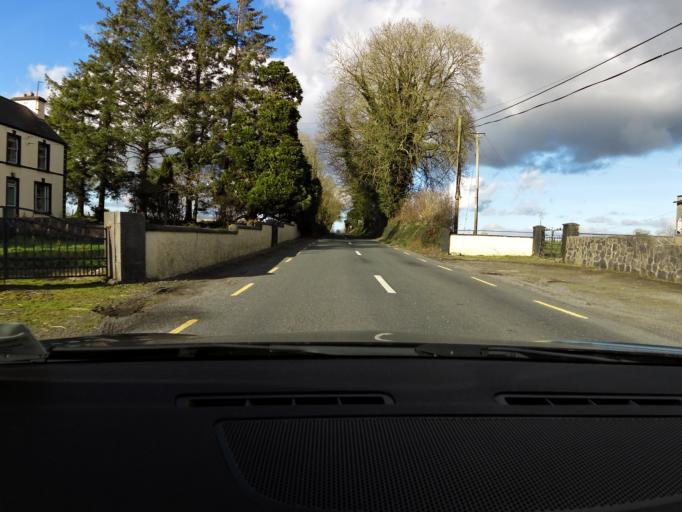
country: IE
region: Connaught
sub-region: Roscommon
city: Castlerea
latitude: 53.6755
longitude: -8.4930
